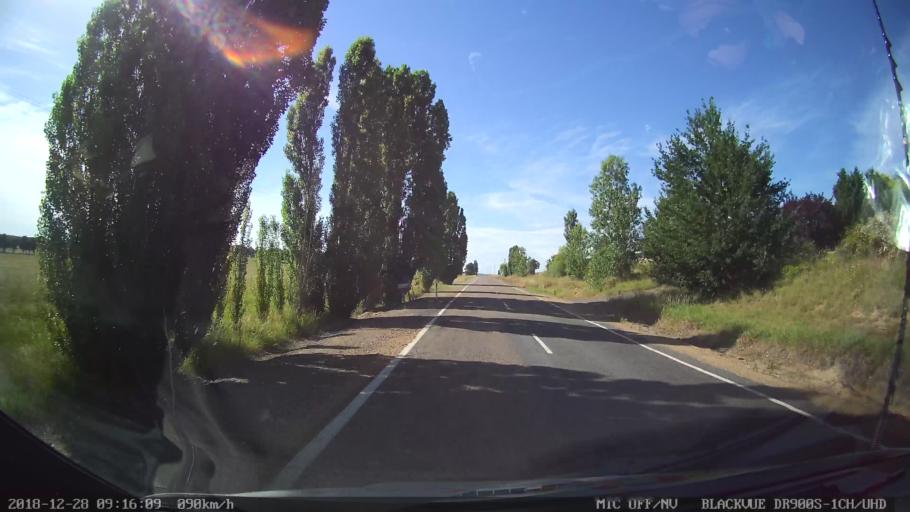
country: AU
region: New South Wales
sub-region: Upper Lachlan Shire
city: Crookwell
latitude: -34.3047
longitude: 149.3541
